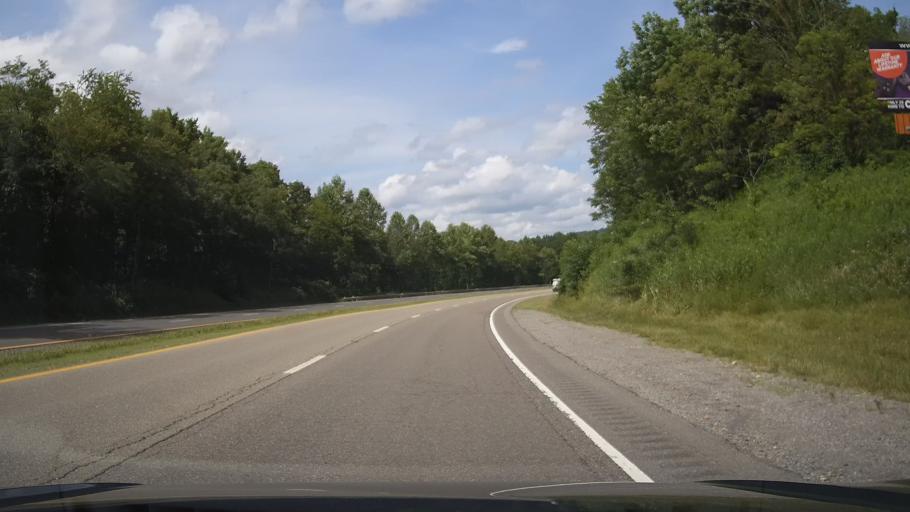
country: US
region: Virginia
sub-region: City of Norton
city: Norton
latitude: 36.9477
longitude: -82.6119
